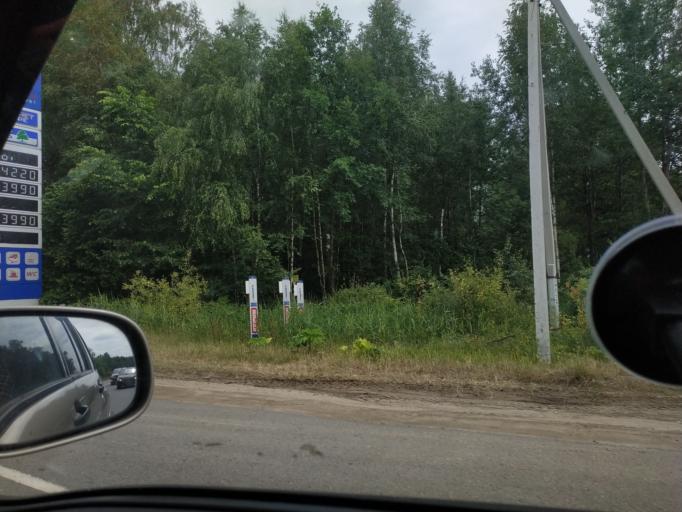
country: RU
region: Moskovskaya
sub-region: Shchelkovskiy Rayon
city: Grebnevo
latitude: 55.9726
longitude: 38.0918
